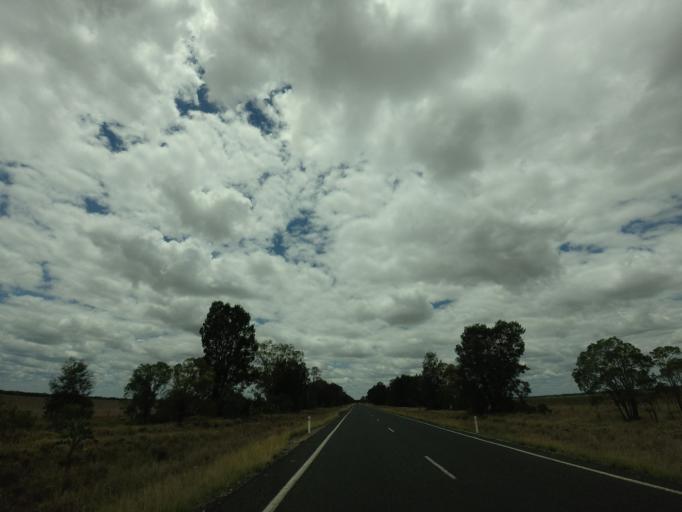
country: AU
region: Queensland
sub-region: Goondiwindi
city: Goondiwindi
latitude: -28.1669
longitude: 150.5247
